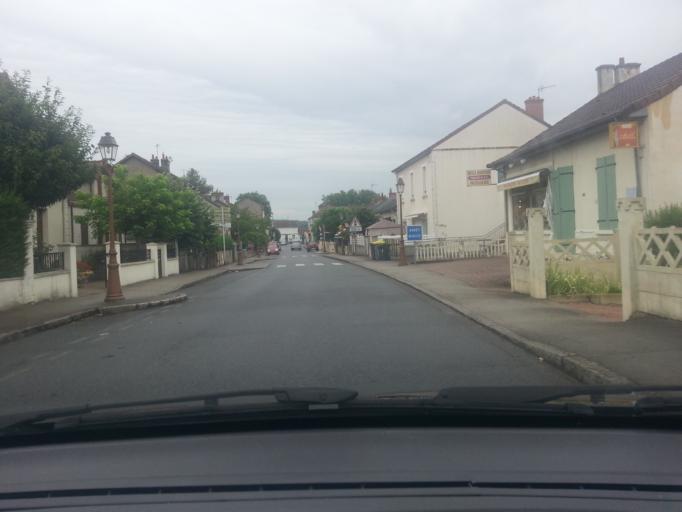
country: FR
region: Bourgogne
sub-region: Departement de Saone-et-Loire
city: Montchanin
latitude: 46.7571
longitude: 4.4793
